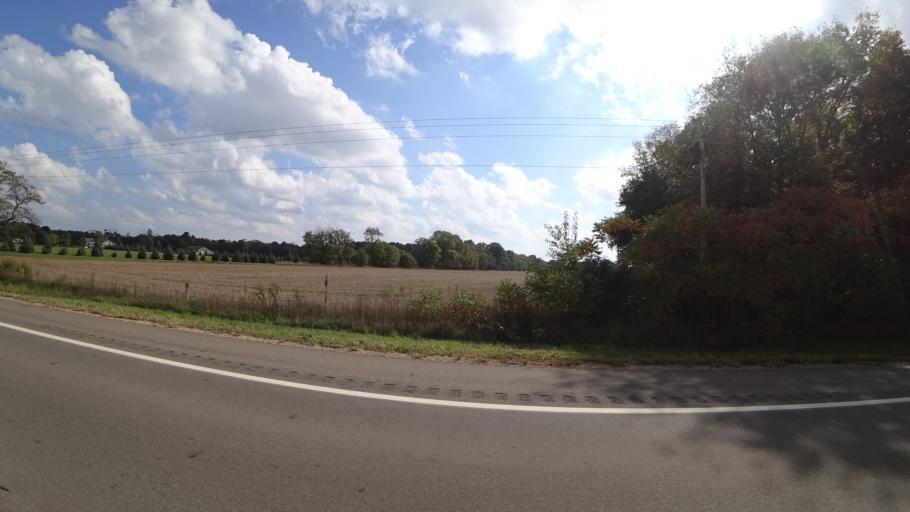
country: US
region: Michigan
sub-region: Branch County
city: Union City
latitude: 42.0678
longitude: -85.1775
